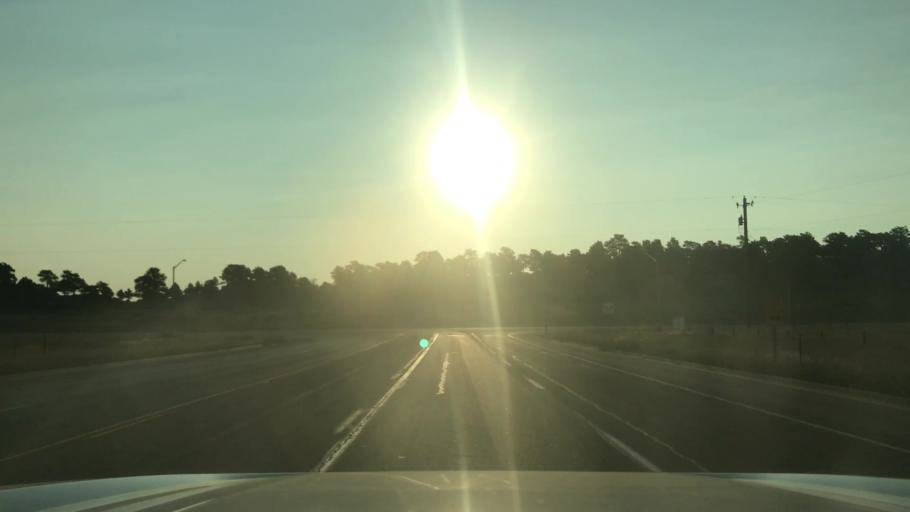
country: US
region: Wyoming
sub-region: Natrona County
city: Evansville
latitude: 42.8400
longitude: -106.2182
